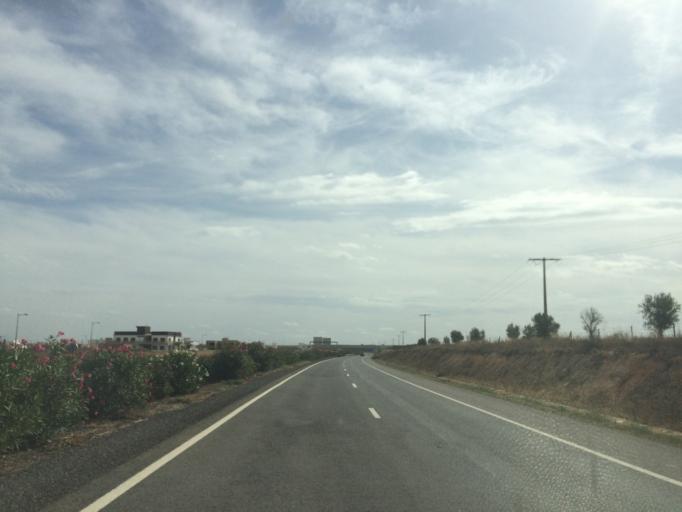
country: MA
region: Meknes-Tafilalet
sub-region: Meknes
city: Meknes
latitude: 33.8431
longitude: -5.6015
